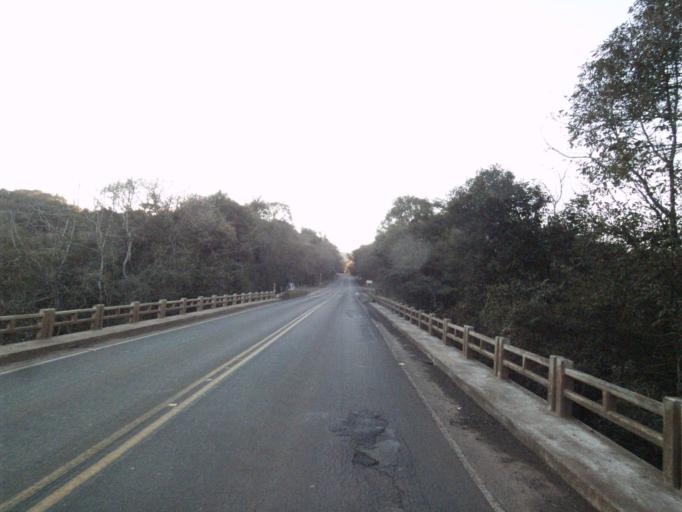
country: BR
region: Santa Catarina
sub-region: Chapeco
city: Chapeco
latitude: -26.8299
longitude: -53.0456
